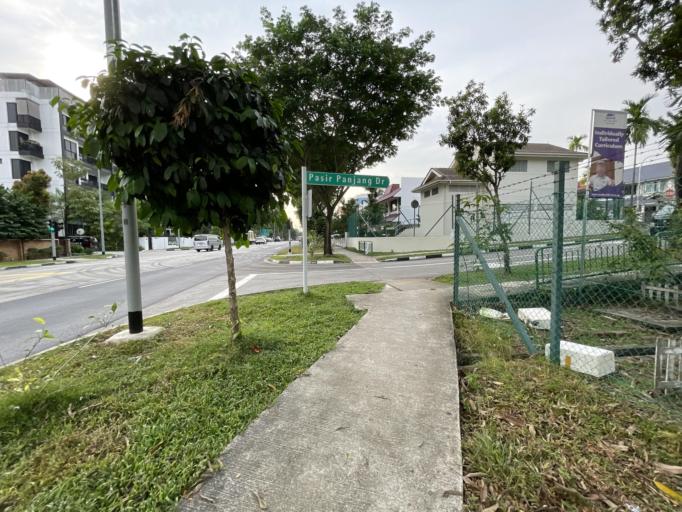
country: SG
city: Singapore
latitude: 1.2915
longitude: 103.7710
